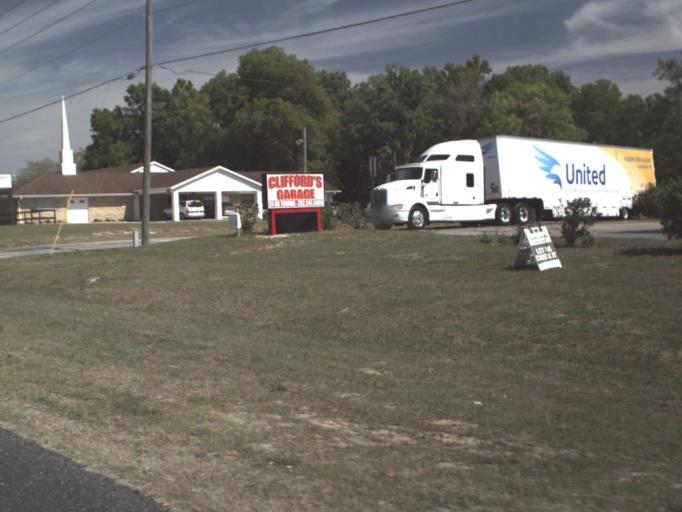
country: US
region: Florida
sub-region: Marion County
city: Belleview
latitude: 29.0420
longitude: -82.0312
